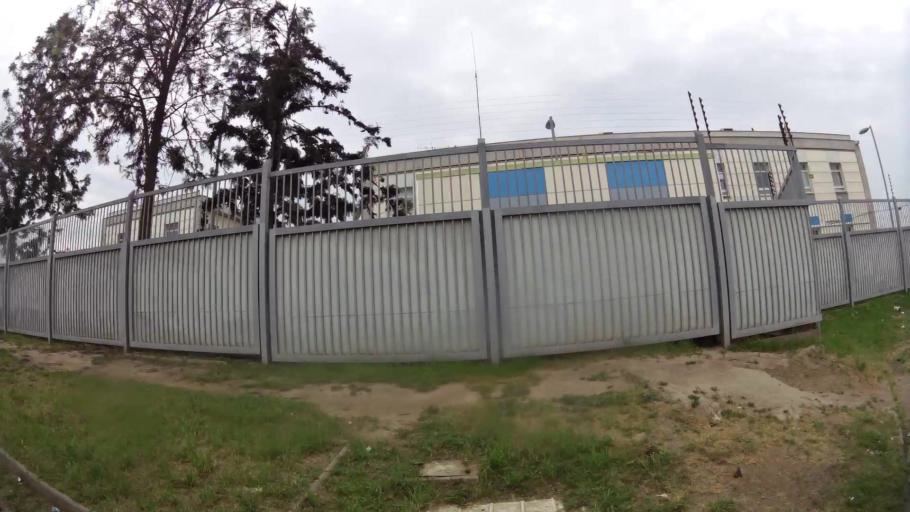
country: CL
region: Santiago Metropolitan
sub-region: Provincia de Santiago
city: Villa Presidente Frei, Nunoa, Santiago, Chile
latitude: -33.4765
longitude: -70.5932
